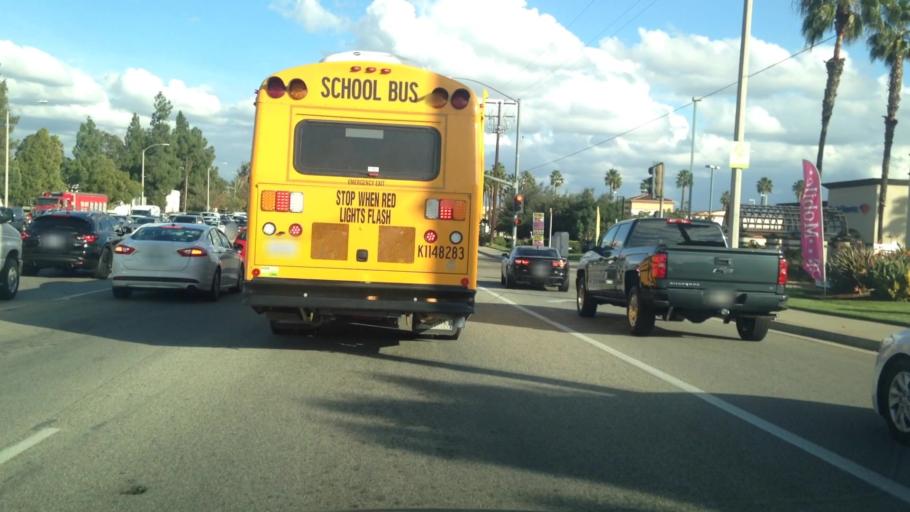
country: US
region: California
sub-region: Riverside County
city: Woodcrest
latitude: 33.9163
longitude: -117.3273
